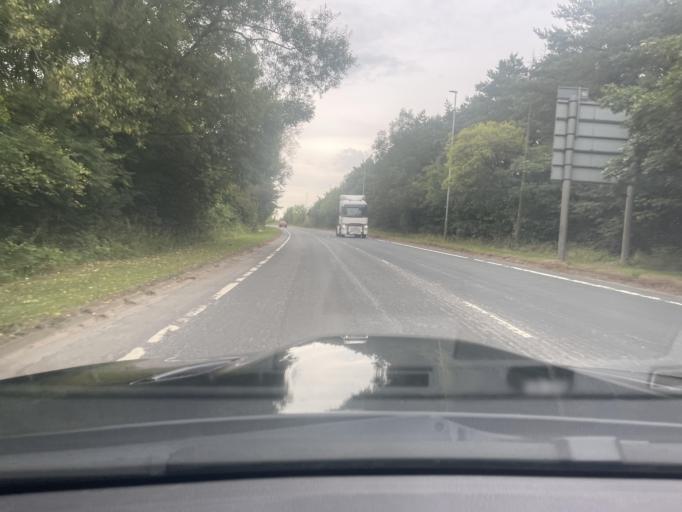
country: GB
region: England
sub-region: Lancashire
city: Leyland
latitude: 53.7020
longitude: -2.7175
